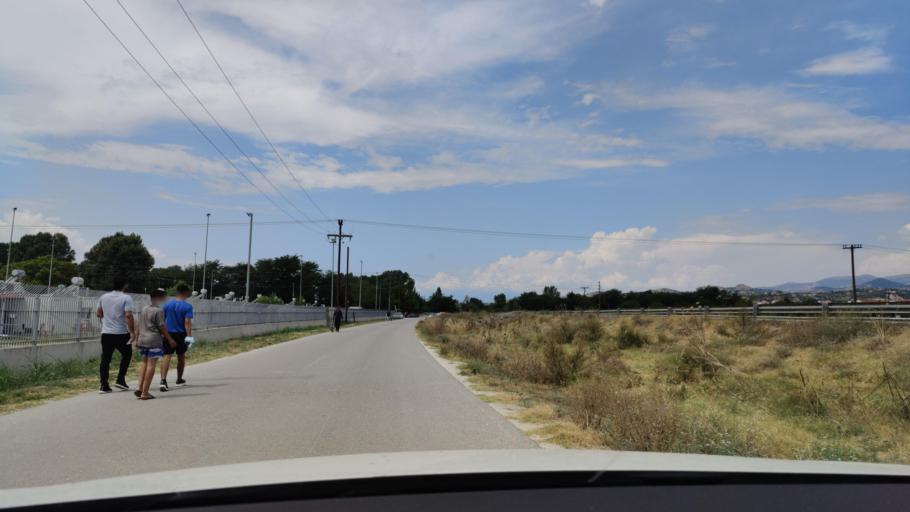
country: GR
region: Central Macedonia
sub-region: Nomos Serron
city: Serres
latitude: 41.0724
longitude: 23.5496
